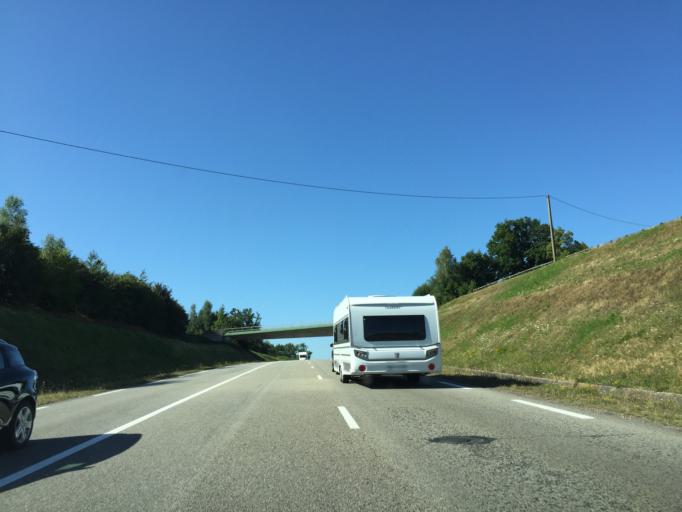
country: FR
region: Lower Normandy
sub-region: Departement du Calvados
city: Lisieux
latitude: 49.1888
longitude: 0.2288
